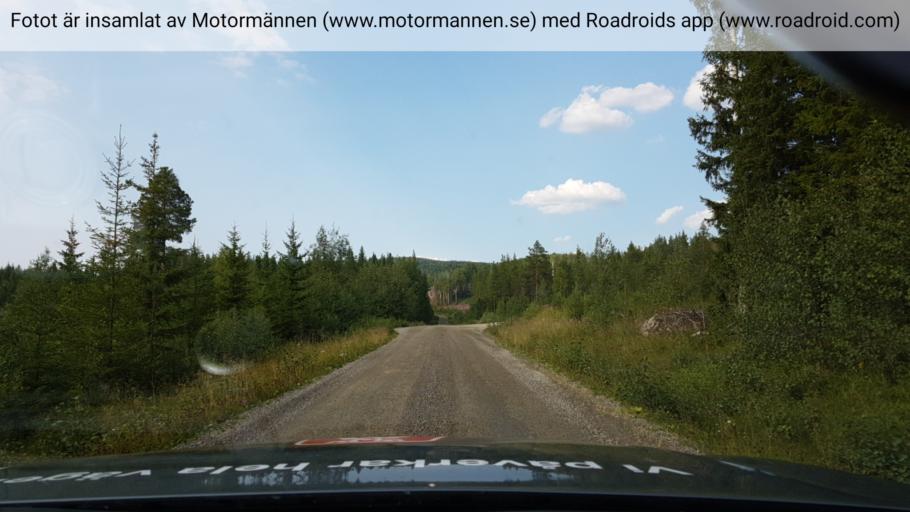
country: SE
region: Jaemtland
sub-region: Bergs Kommun
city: Hoverberg
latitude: 62.5228
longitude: 14.9136
